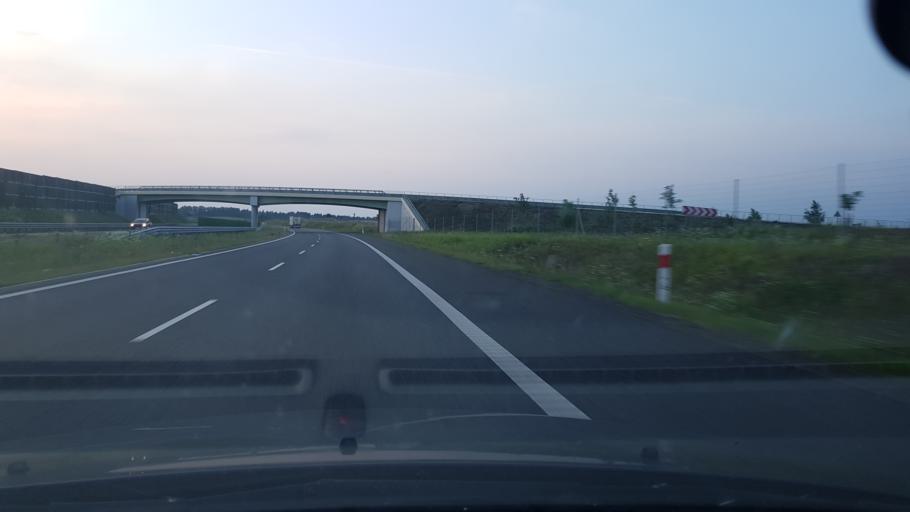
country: PL
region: Warmian-Masurian Voivodeship
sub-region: Powiat nidzicki
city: Nidzica
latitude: 53.4360
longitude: 20.3404
